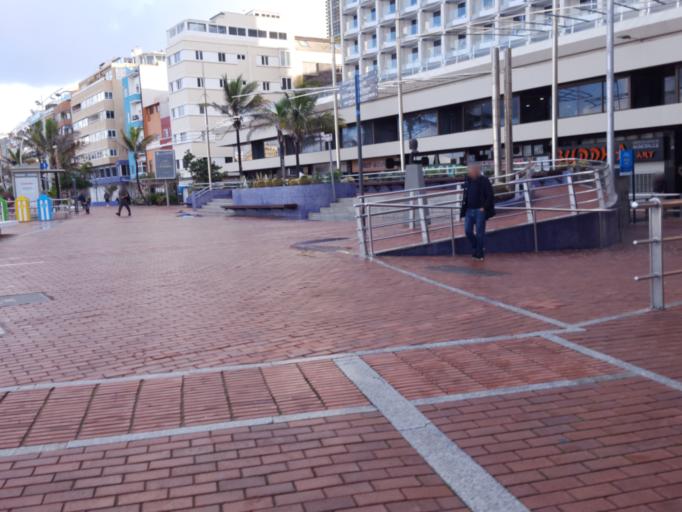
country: ES
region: Canary Islands
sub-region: Provincia de Las Palmas
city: Las Palmas de Gran Canaria
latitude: 28.1446
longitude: -15.4313
